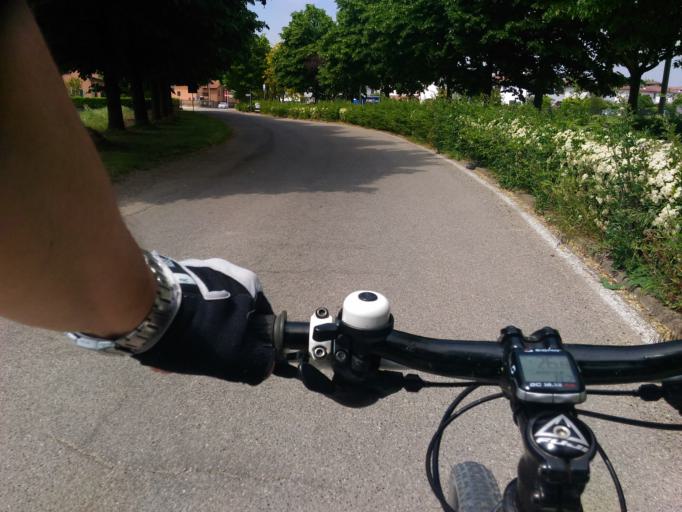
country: IT
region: Lombardy
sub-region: Provincia di Lodi
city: Casalmaiocco
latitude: 45.3523
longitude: 9.3781
